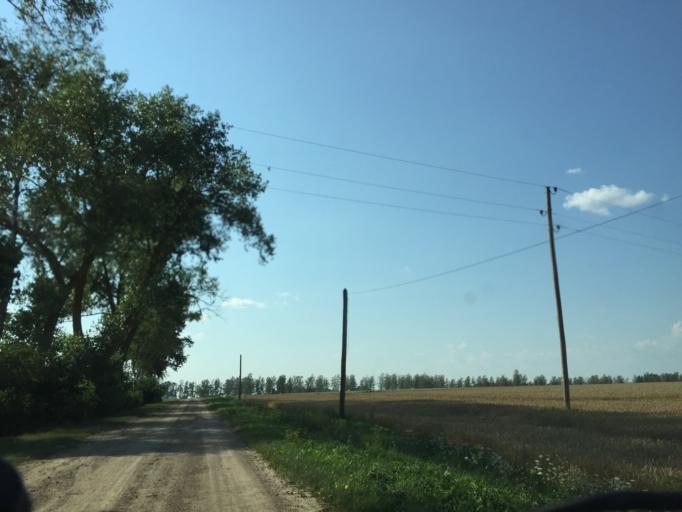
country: LV
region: Jelgava
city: Jelgava
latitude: 56.4705
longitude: 23.7014
